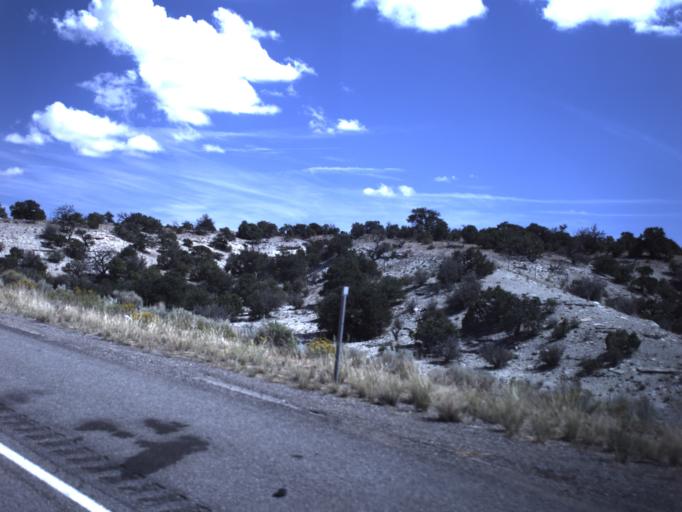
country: US
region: Utah
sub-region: Emery County
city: Ferron
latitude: 38.8413
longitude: -110.9579
